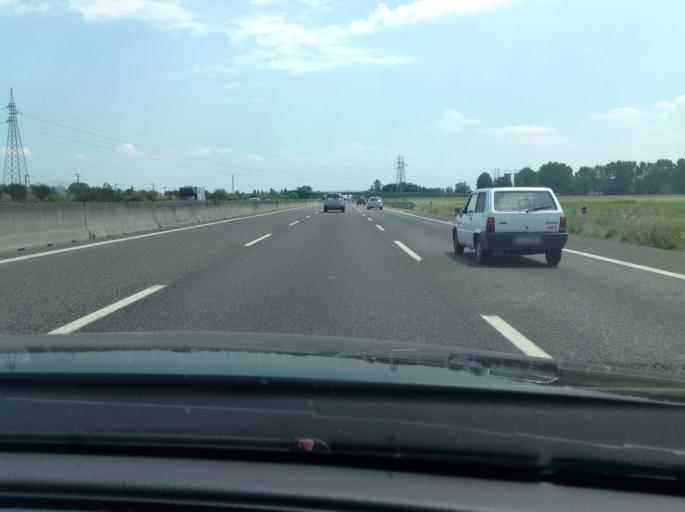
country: IT
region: Lombardy
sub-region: Provincia di Lodi
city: Somaglia
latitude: 45.1526
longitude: 9.6200
